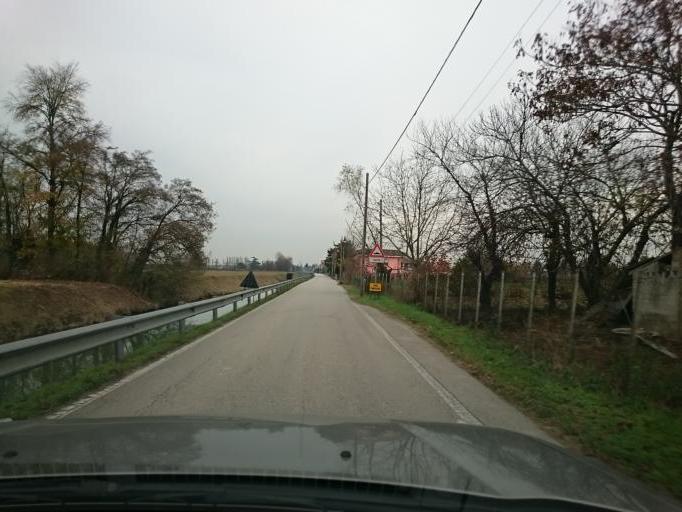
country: IT
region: Veneto
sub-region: Provincia di Padova
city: Tencarola
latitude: 45.3985
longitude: 11.8228
